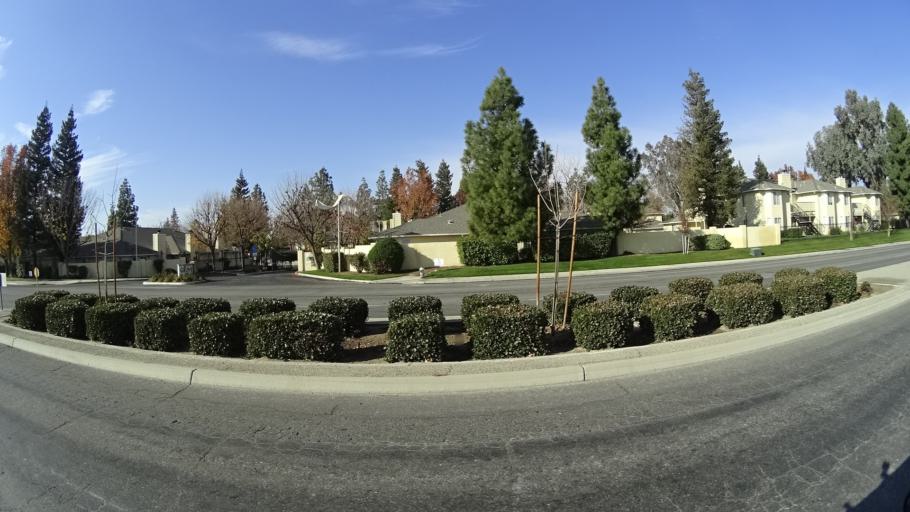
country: US
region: California
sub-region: Kern County
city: Greenacres
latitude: 35.4032
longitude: -119.0743
